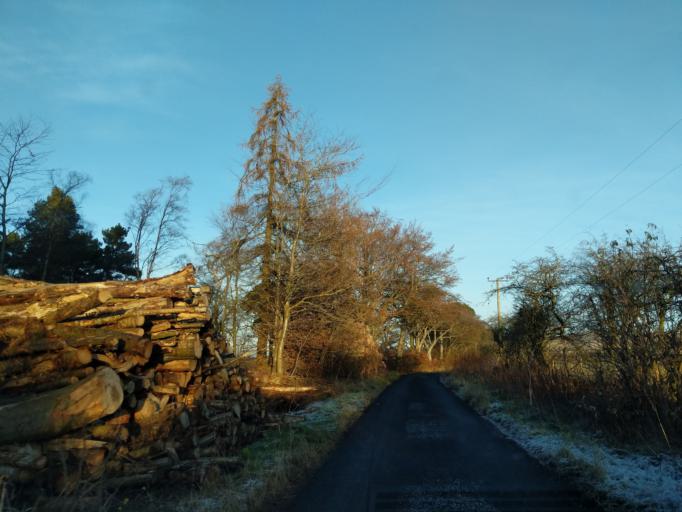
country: GB
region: Scotland
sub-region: Edinburgh
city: Balerno
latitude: 55.8604
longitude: -3.3477
